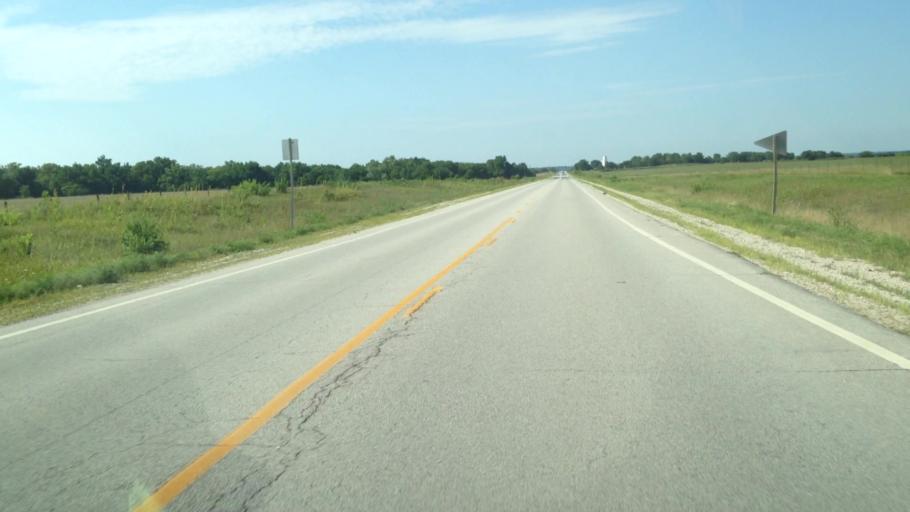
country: US
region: Kansas
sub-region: Neosho County
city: Erie
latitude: 37.4867
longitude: -95.2692
